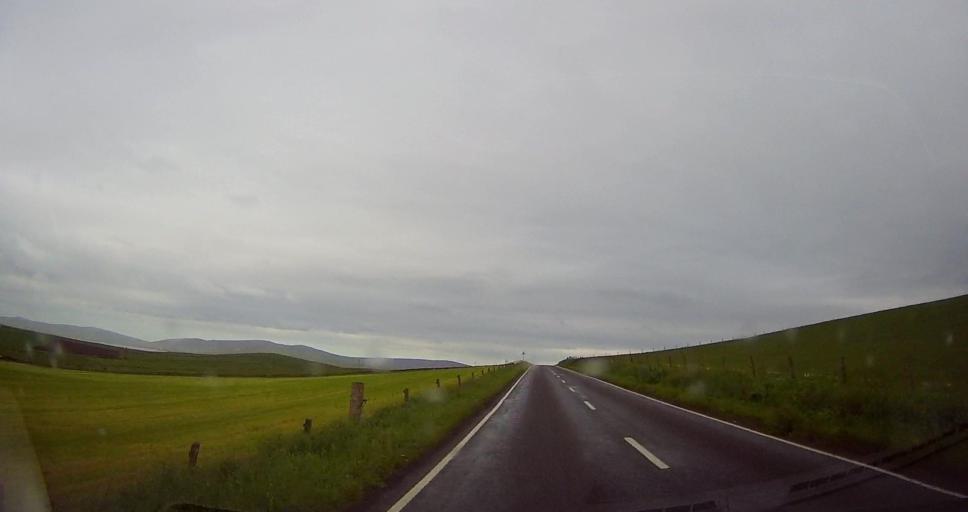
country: GB
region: Scotland
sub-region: Orkney Islands
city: Stromness
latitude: 59.0035
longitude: -3.2869
